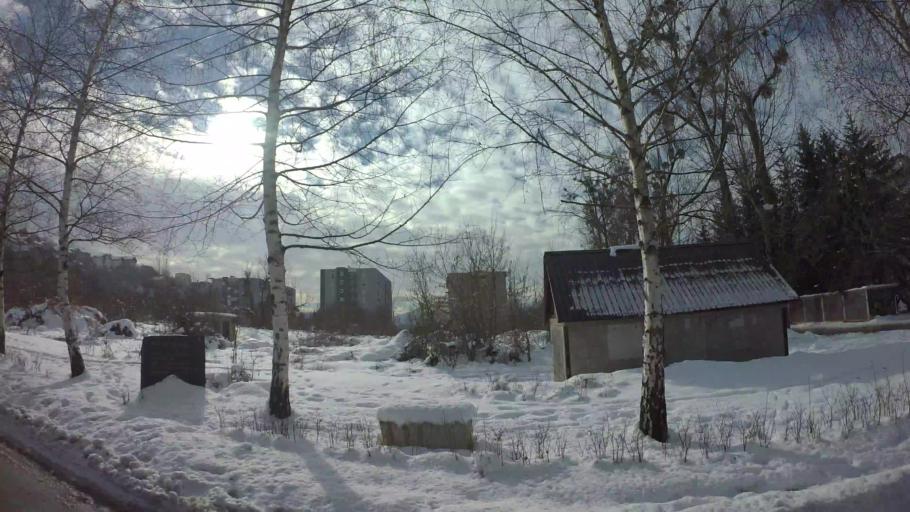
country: BA
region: Federation of Bosnia and Herzegovina
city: Kobilja Glava
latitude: 43.8819
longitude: 18.4152
